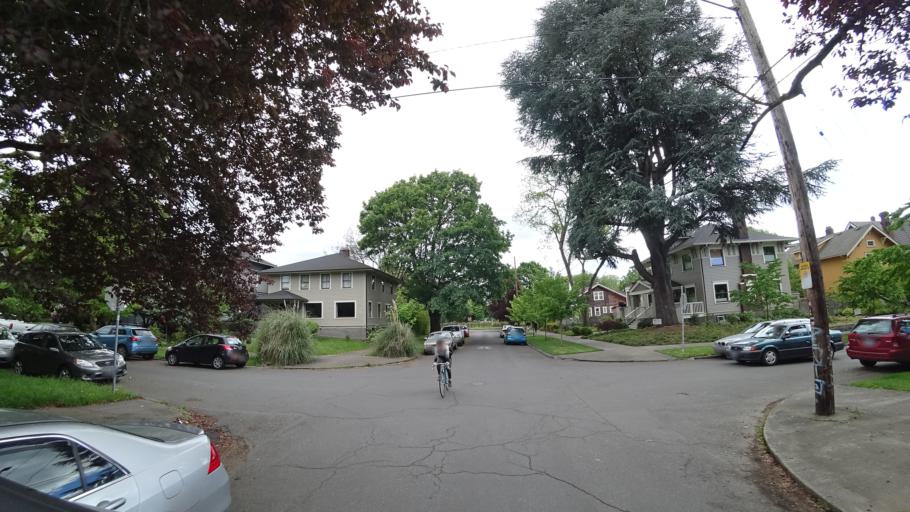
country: US
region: Oregon
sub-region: Multnomah County
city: Portland
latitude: 45.5114
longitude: -122.6494
